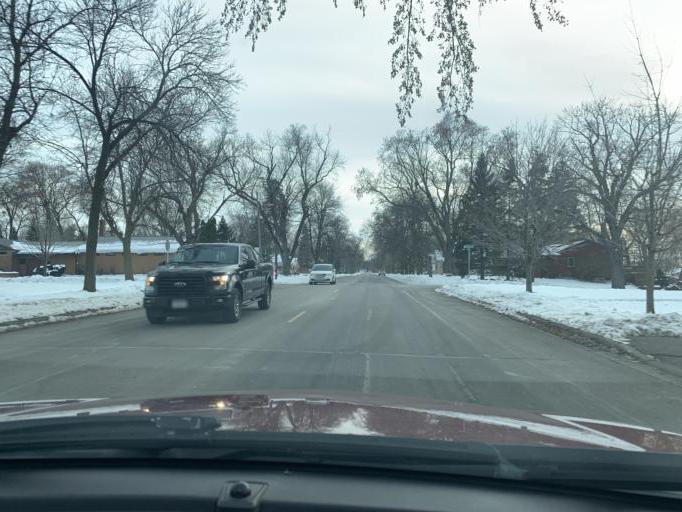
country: US
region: Minnesota
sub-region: Washington County
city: Saint Paul Park
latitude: 44.8464
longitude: -92.9915
